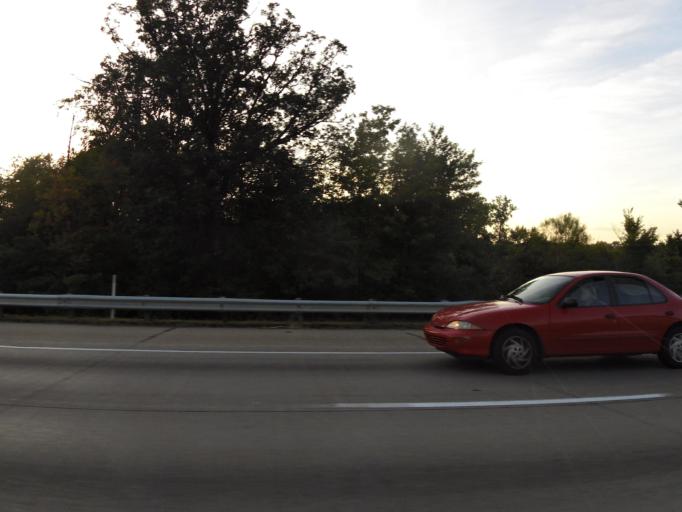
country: US
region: Indiana
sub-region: Marion County
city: Warren Park
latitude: 39.7569
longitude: -86.0294
